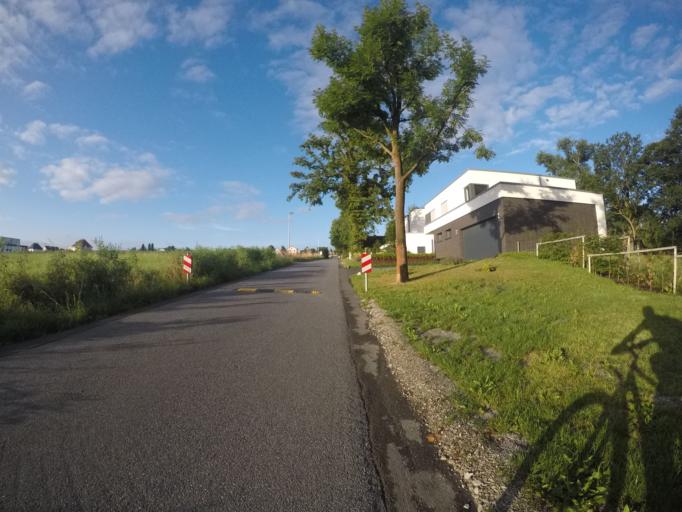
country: DE
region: North Rhine-Westphalia
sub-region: Regierungsbezirk Detmold
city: Hiddenhausen
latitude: 52.1328
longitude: 8.6294
